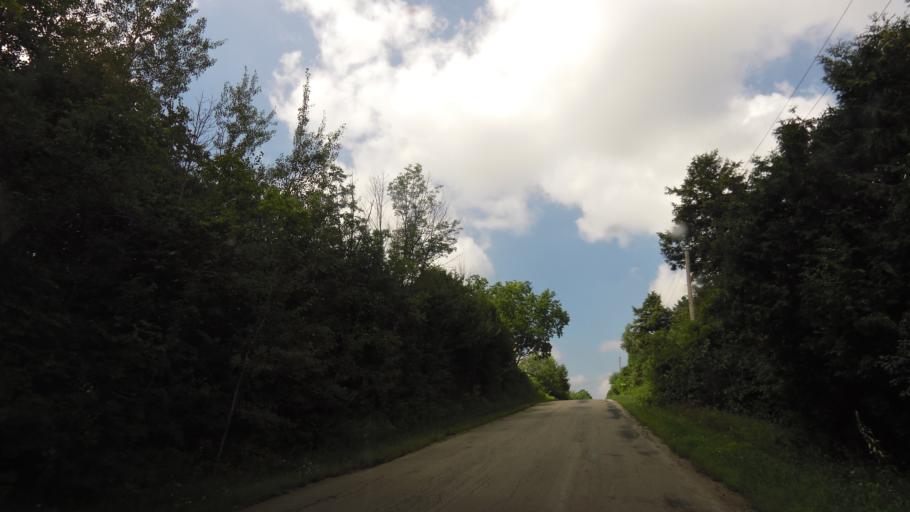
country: CA
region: Ontario
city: Oshawa
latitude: 43.9990
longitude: -78.8756
